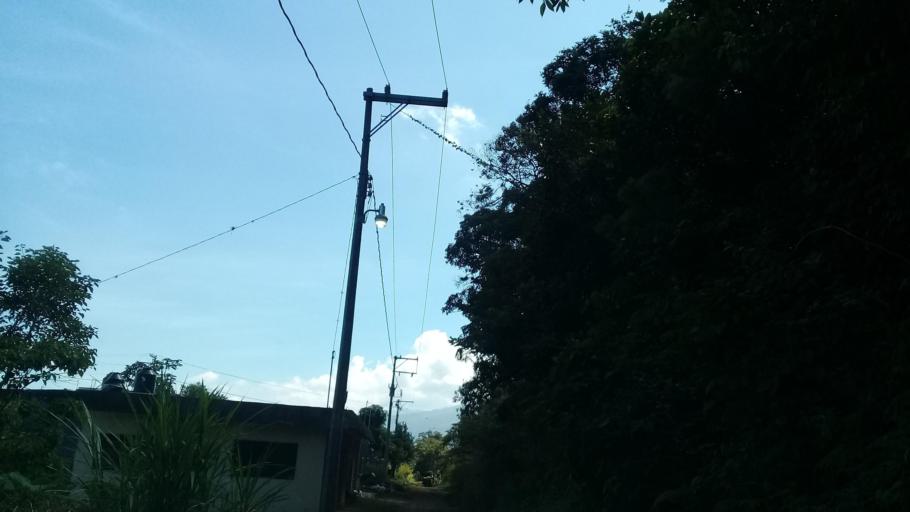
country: MX
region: Veracruz
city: Amatlan de los Reyes
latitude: 18.8368
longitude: -96.9213
